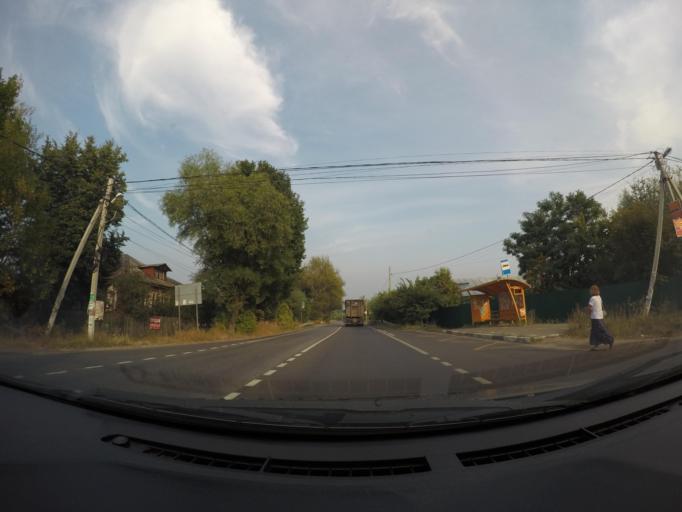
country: RU
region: Moskovskaya
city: Rechitsy
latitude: 55.5807
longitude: 38.5631
